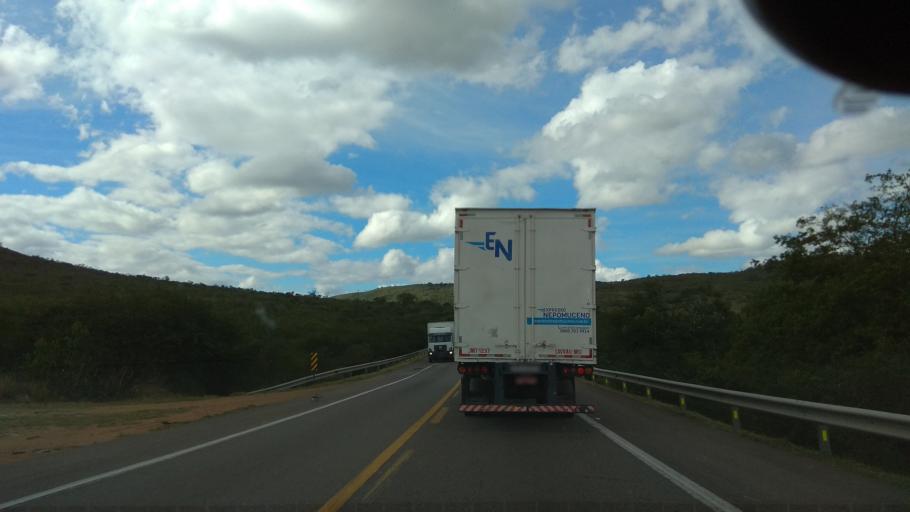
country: BR
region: Bahia
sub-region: Amargosa
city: Amargosa
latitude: -12.9159
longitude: -39.8700
